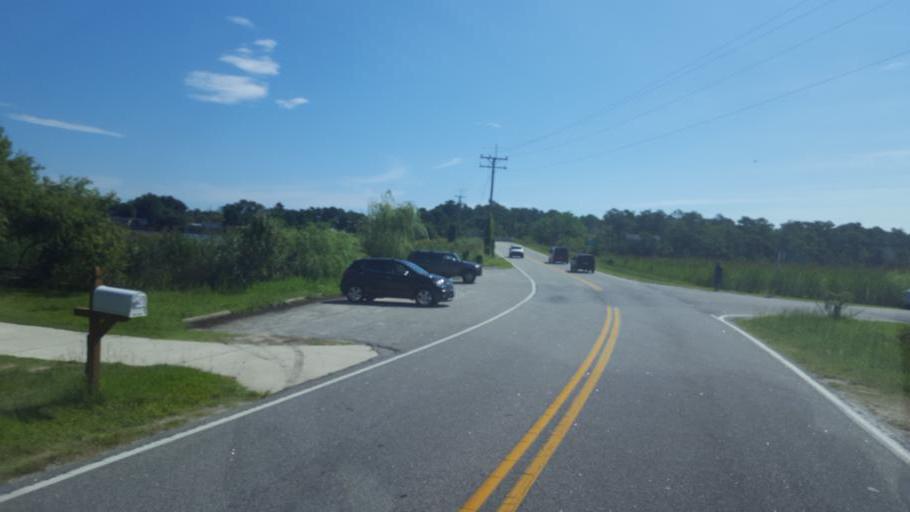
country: US
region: North Carolina
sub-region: Dare County
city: Kill Devil Hills
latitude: 36.0085
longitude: -75.7022
